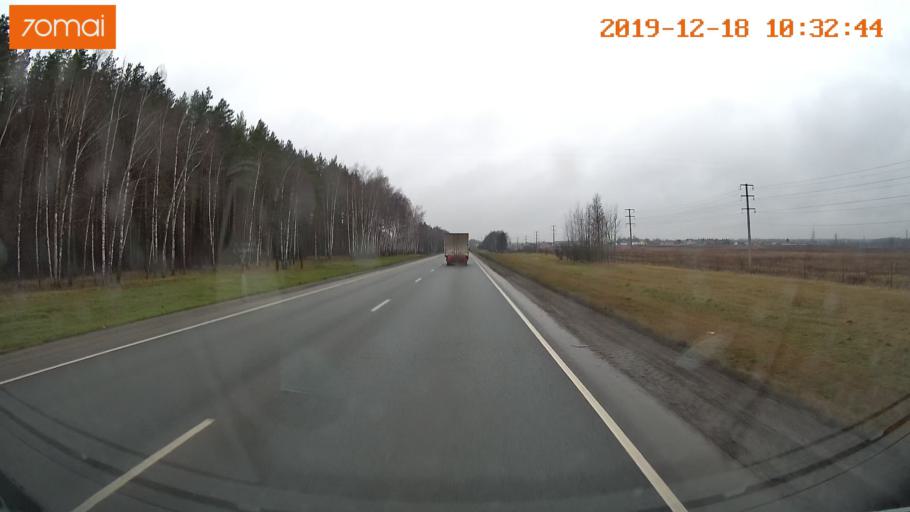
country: RU
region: Moskovskaya
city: Troitsk
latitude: 55.4003
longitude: 37.2294
